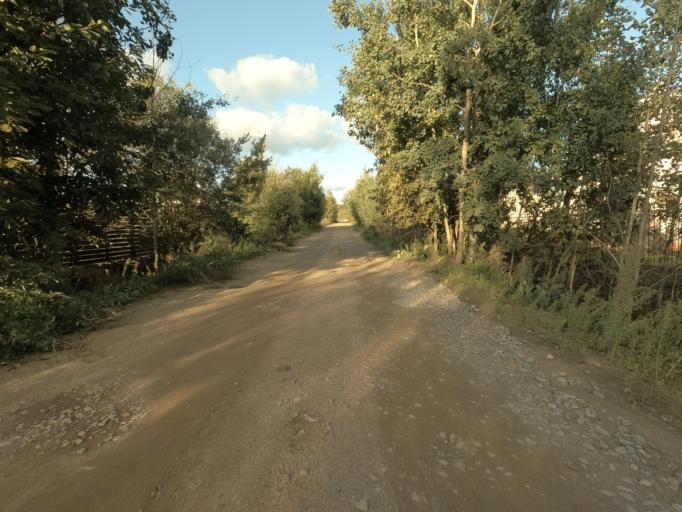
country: RU
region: Leningrad
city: Otradnoye
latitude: 59.8698
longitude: 30.7751
